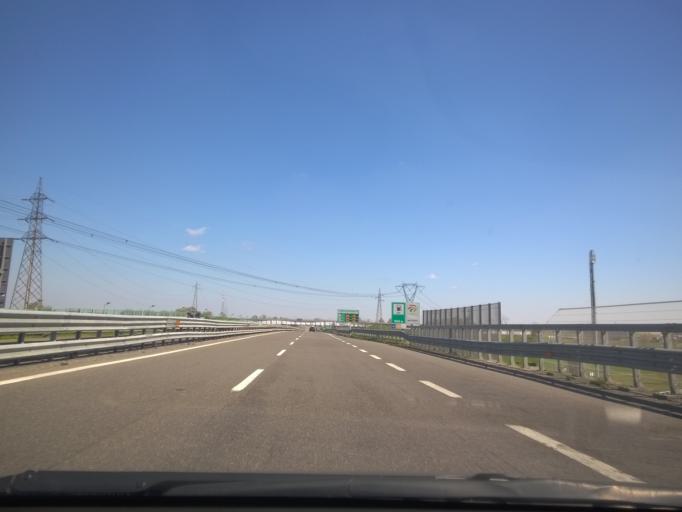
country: IT
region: Emilia-Romagna
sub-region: Provincia di Piacenza
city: Piacenza
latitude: 45.0519
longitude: 9.7499
